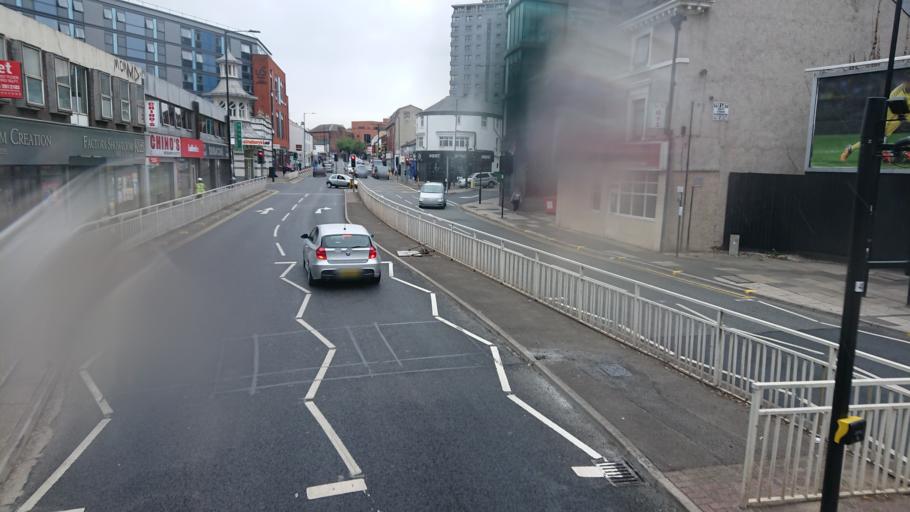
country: GB
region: England
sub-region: Sheffield
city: Sheffield
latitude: 53.3728
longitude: -1.4768
